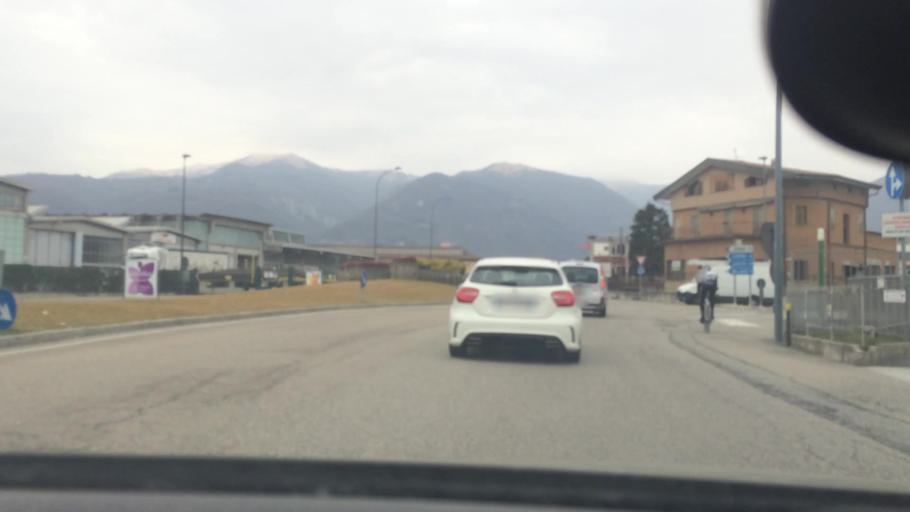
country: IT
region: Lombardy
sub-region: Provincia di Como
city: Merone
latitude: 45.7953
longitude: 9.2416
